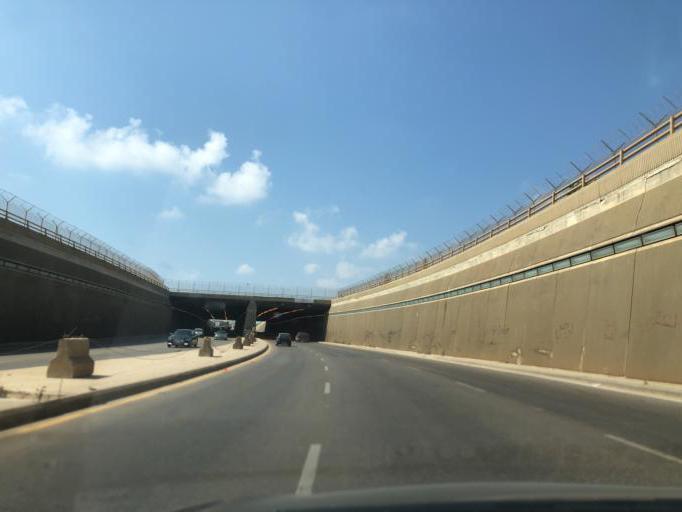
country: LB
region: Mont-Liban
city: Baabda
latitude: 33.8208
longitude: 35.4865
